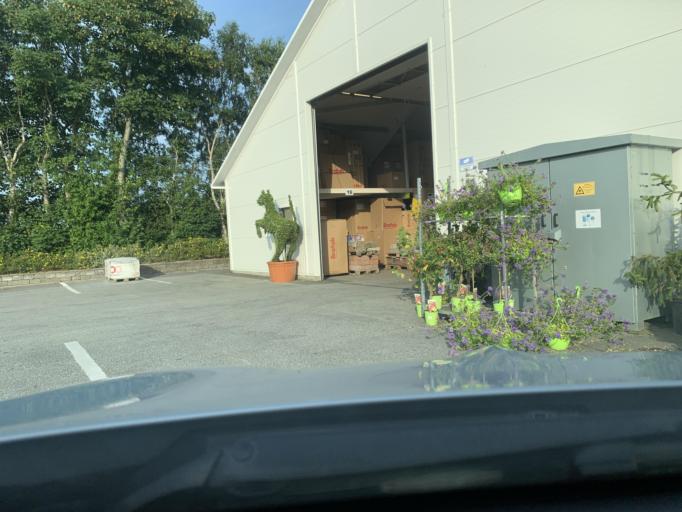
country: NO
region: Rogaland
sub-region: Time
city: Bryne
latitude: 58.7381
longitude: 5.6119
